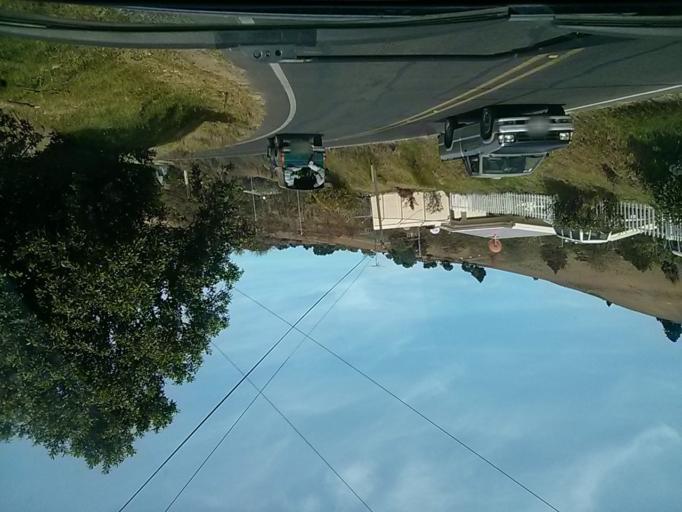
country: CR
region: Cartago
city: Cot
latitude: 9.9234
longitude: -83.8807
